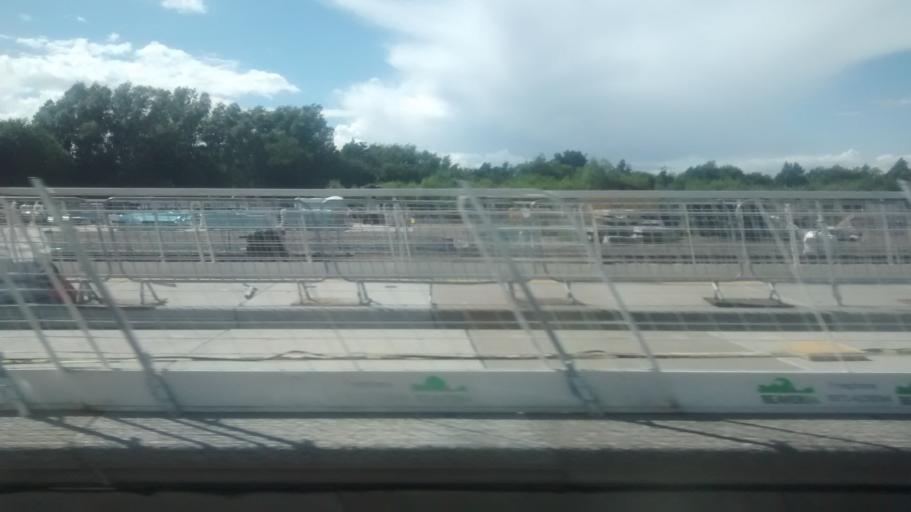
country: GB
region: England
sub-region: Cambridgeshire
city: Cambridge
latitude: 52.2243
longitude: 0.1588
